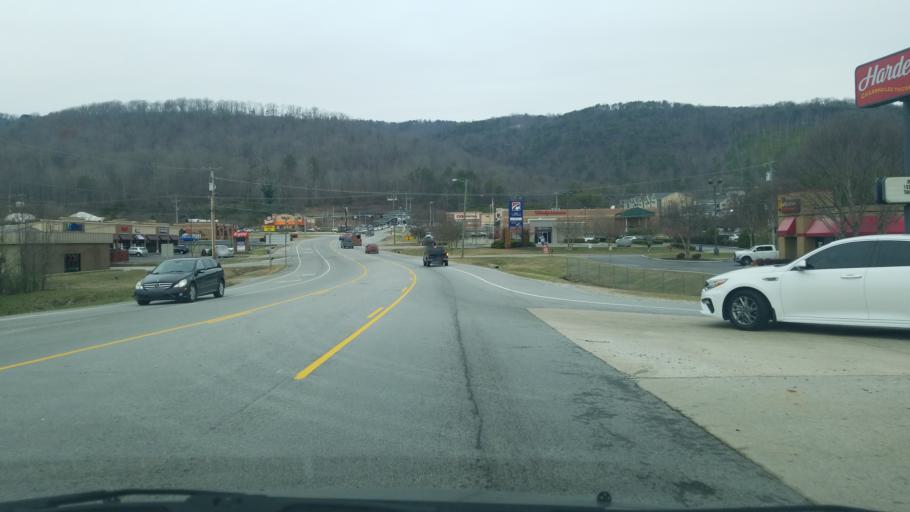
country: US
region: Tennessee
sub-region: Hamilton County
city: Soddy-Daisy
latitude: 35.2356
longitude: -85.1971
